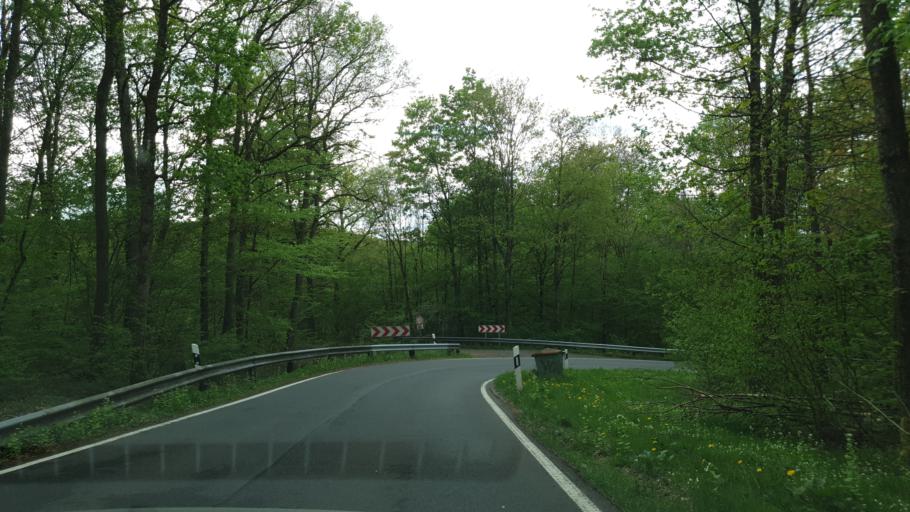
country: DE
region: Rheinland-Pfalz
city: Hardt
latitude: 50.6210
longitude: 7.9124
